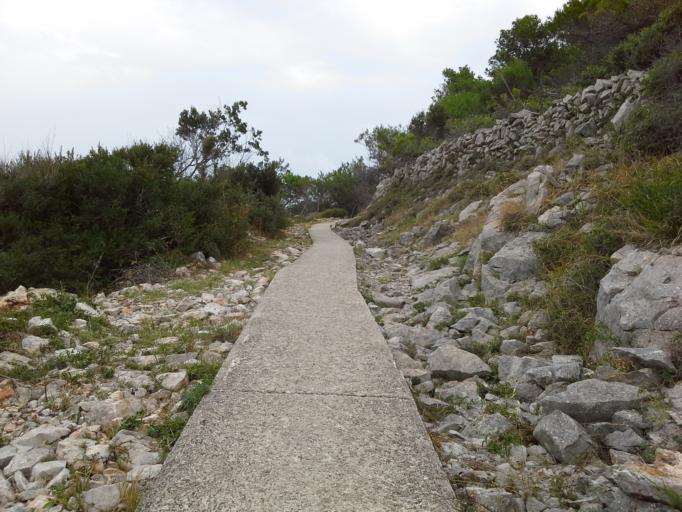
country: HR
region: Primorsko-Goranska
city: Mali Losinj
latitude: 44.5408
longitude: 14.4685
